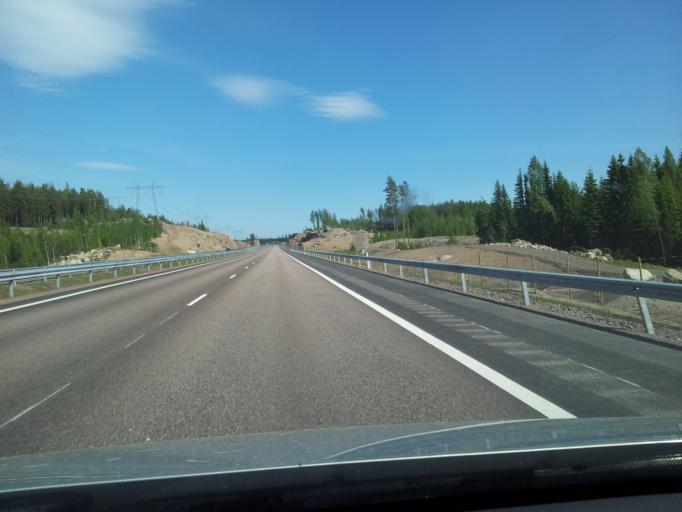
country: FI
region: Uusimaa
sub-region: Loviisa
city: Ruotsinpyhtaeae
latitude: 60.4887
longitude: 26.3518
